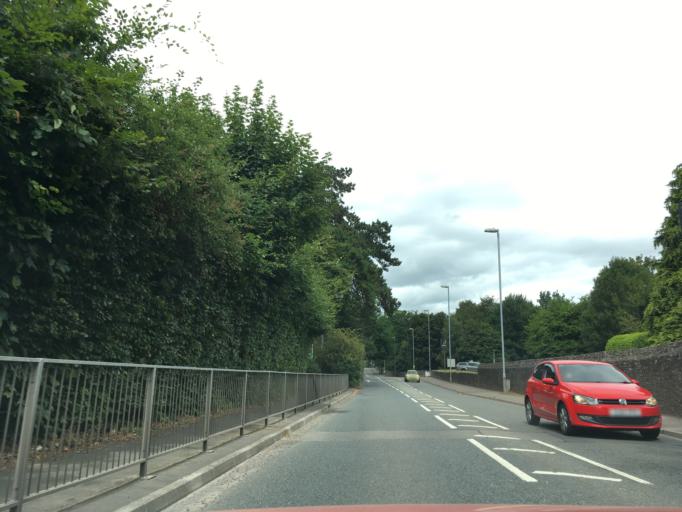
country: GB
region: Wales
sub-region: Monmouthshire
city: Abergavenny
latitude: 51.8129
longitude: -3.0108
